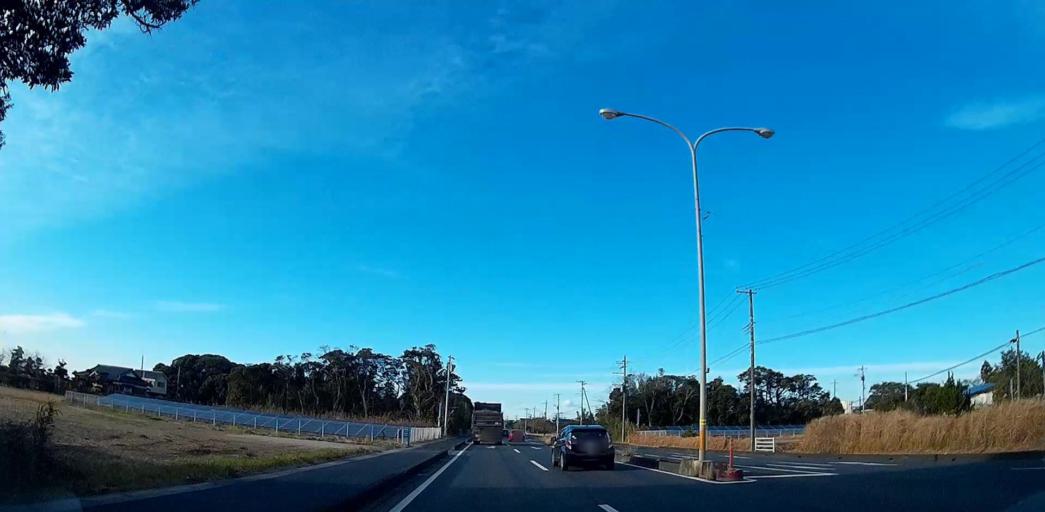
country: JP
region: Chiba
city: Omigawa
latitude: 35.8336
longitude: 140.7188
